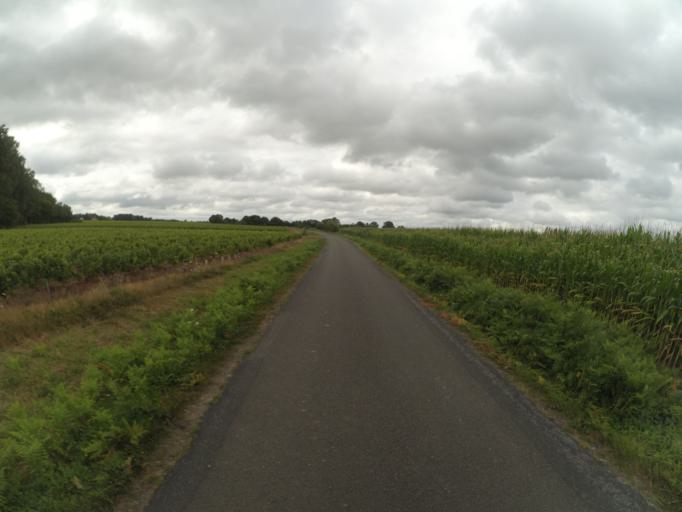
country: FR
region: Pays de la Loire
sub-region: Departement de la Vendee
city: Saint-Philbert-de-Bouaine
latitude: 47.0014
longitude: -1.5265
